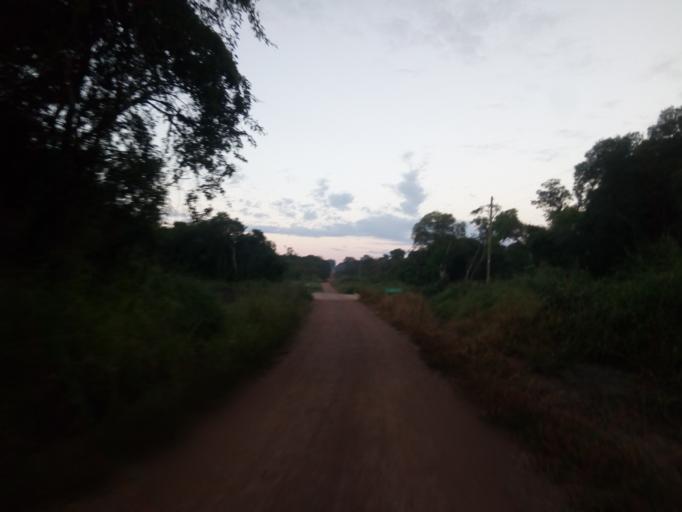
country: AR
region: Misiones
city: Almafuerte
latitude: -27.5657
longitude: -55.4133
